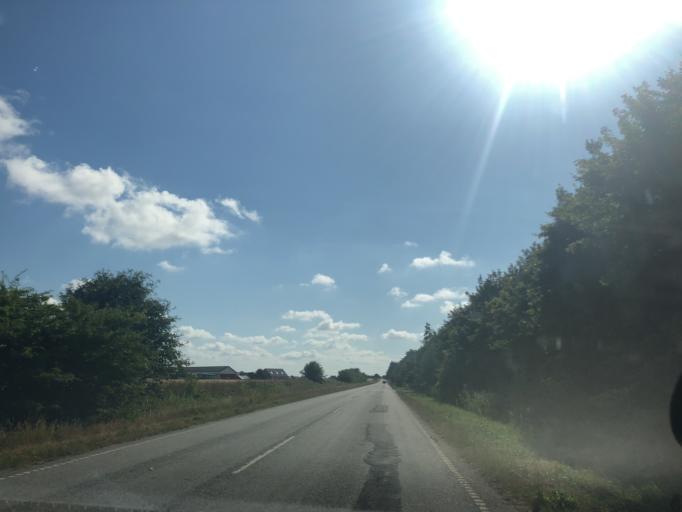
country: DK
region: North Denmark
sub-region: Morso Kommune
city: Nykobing Mors
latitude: 57.0101
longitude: 8.9539
